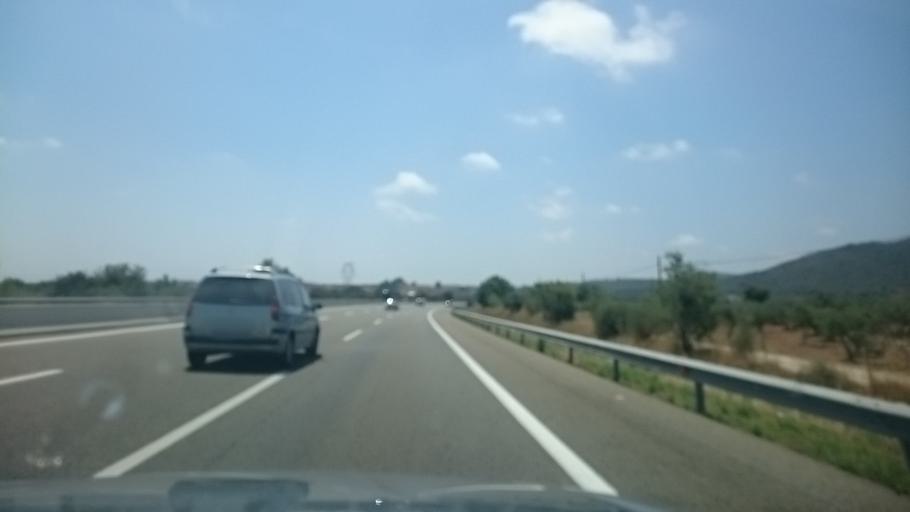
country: ES
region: Catalonia
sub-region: Provincia de Tarragona
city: Santa Oliva
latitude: 41.2485
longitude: 1.5332
